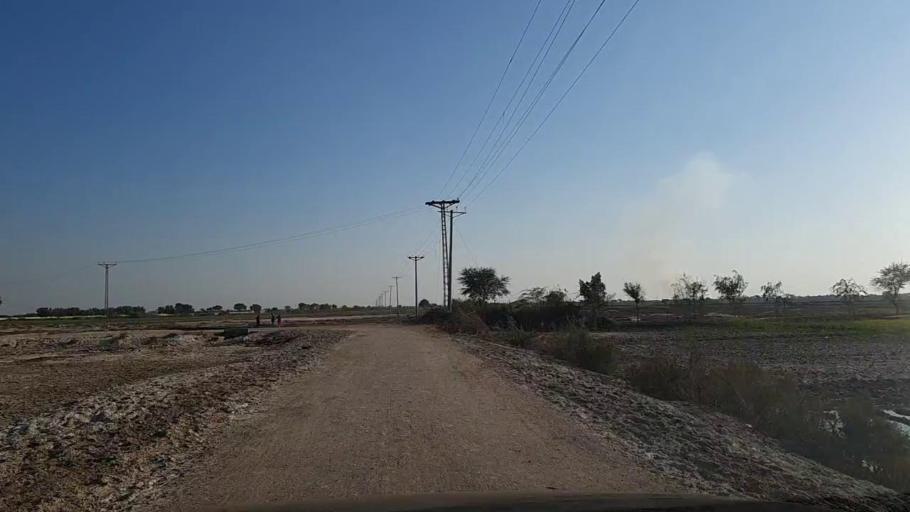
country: PK
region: Sindh
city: Nawabshah
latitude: 26.2015
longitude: 68.3752
